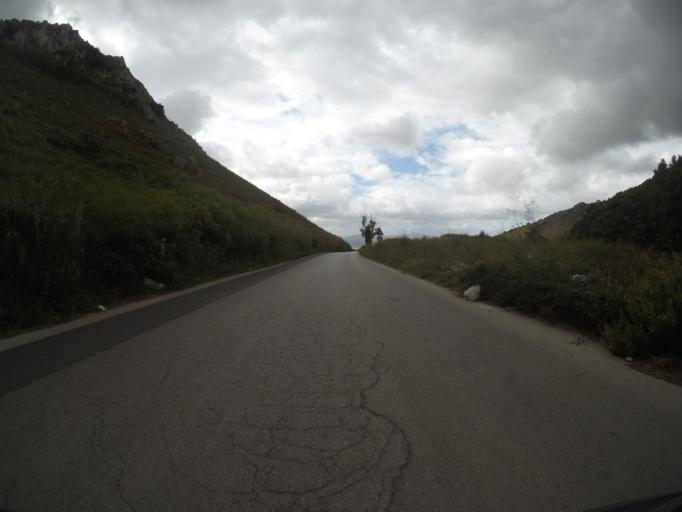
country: IT
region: Sicily
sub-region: Palermo
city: Montelepre
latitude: 38.0992
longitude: 13.1687
